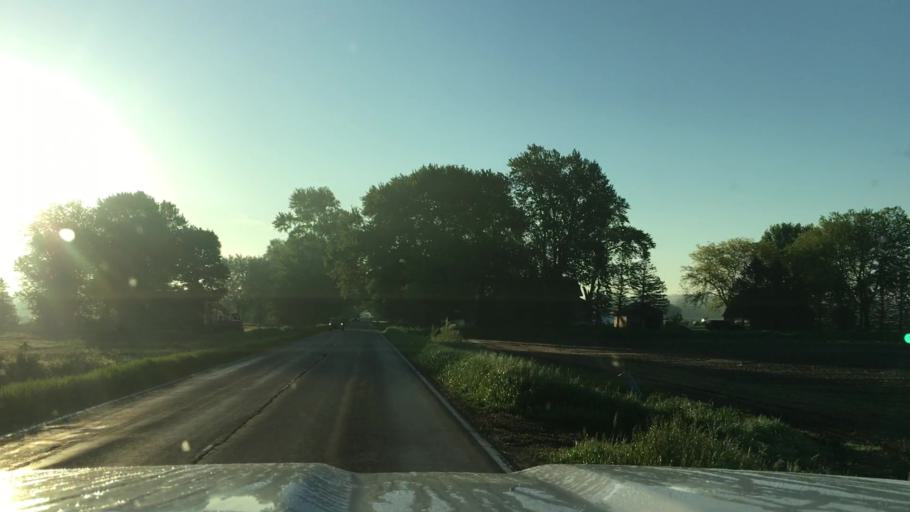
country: US
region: Michigan
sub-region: Kent County
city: Byron Center
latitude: 42.7829
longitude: -85.7340
